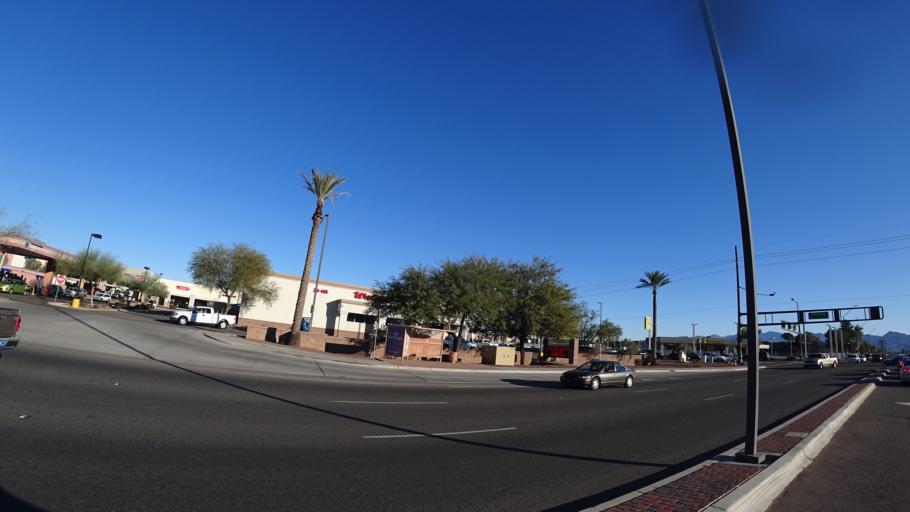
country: US
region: Arizona
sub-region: Maricopa County
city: Avondale
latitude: 33.4506
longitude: -112.3411
